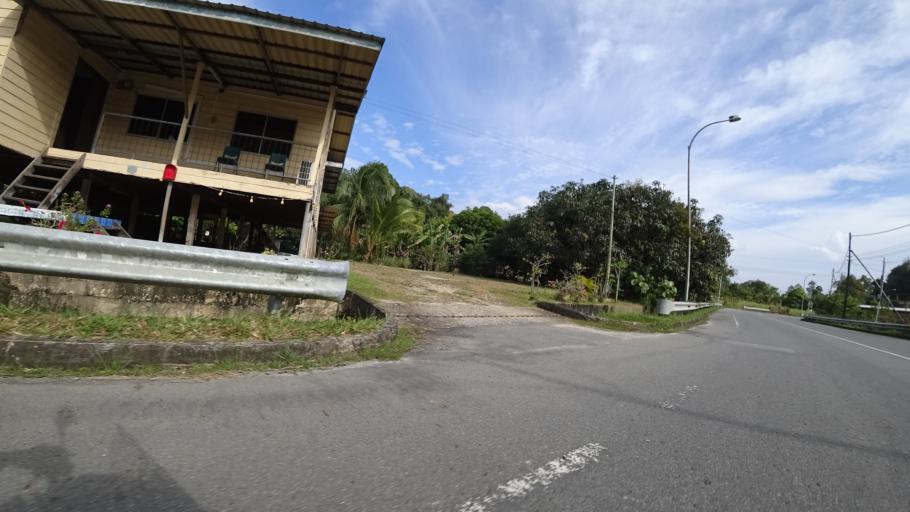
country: BN
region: Brunei and Muara
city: Bandar Seri Begawan
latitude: 4.8780
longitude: 114.8025
